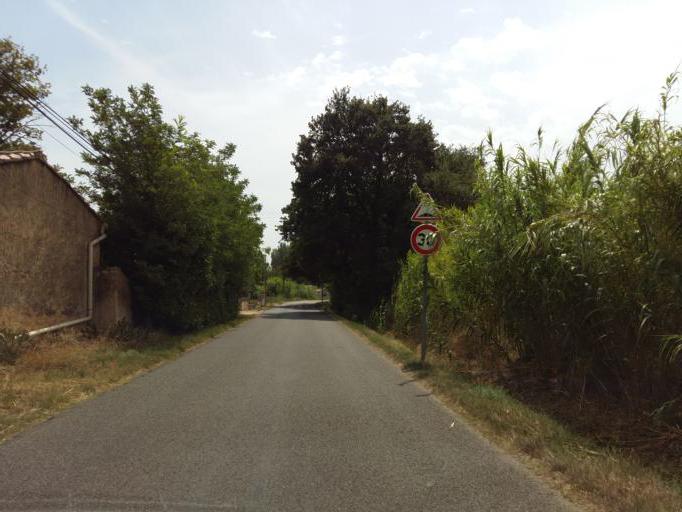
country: FR
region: Provence-Alpes-Cote d'Azur
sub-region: Departement du Vaucluse
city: Piolenc
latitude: 44.1822
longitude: 4.7651
